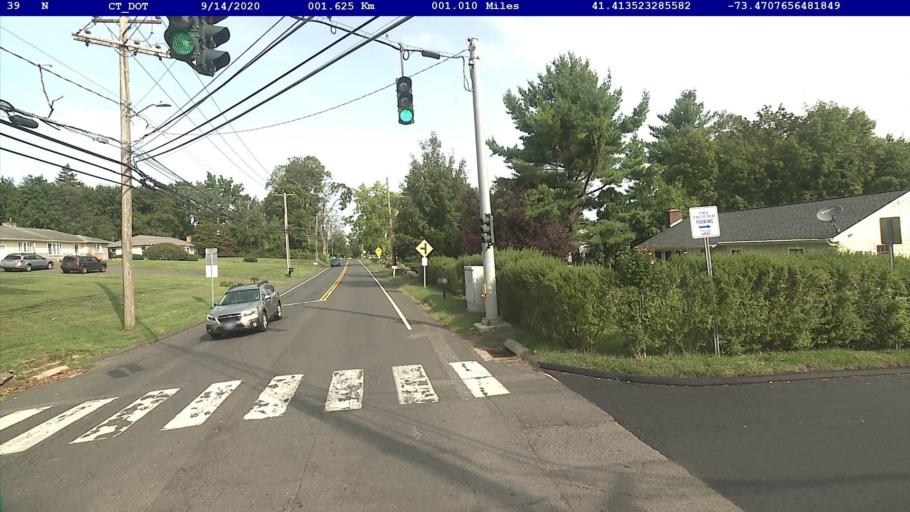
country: US
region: Connecticut
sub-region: Fairfield County
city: Danbury
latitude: 41.4135
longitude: -73.4708
